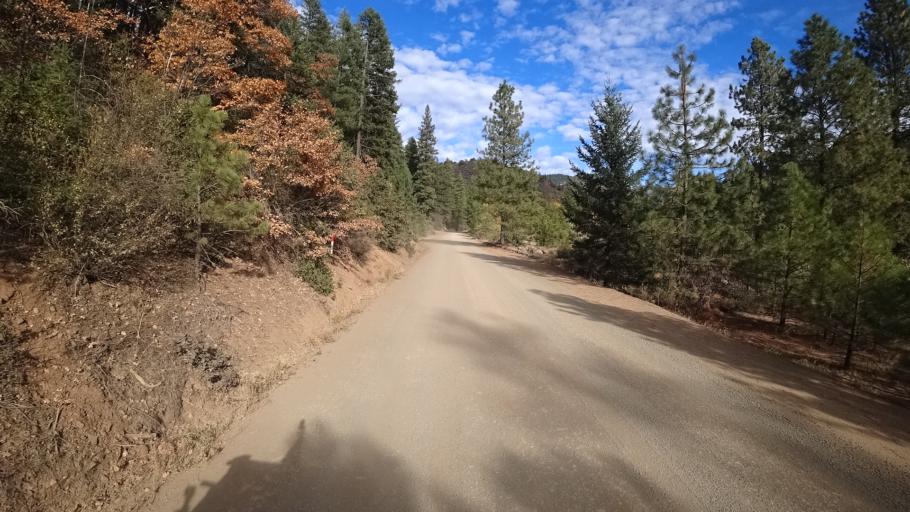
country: US
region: California
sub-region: Siskiyou County
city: Yreka
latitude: 41.6935
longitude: -122.8189
